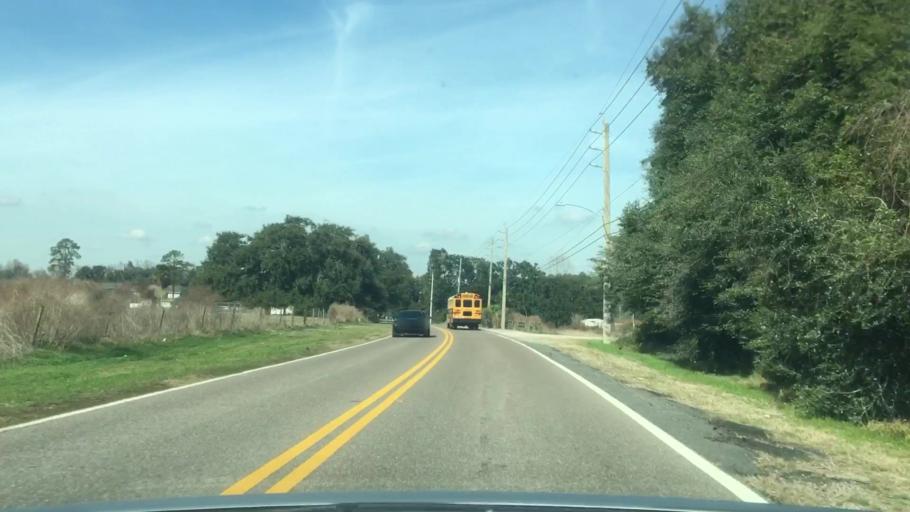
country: US
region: Florida
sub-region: Duval County
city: Jacksonville
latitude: 30.4580
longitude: -81.5589
